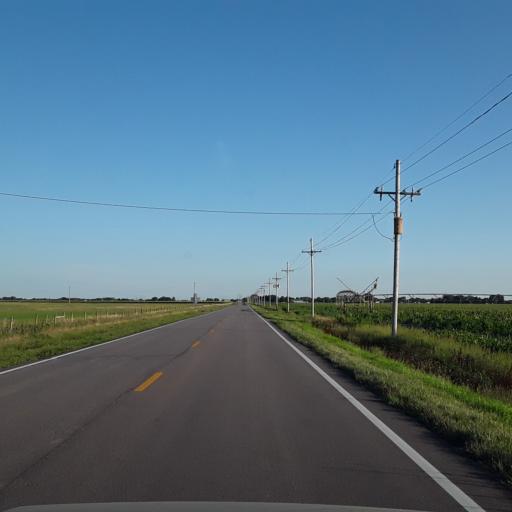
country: US
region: Nebraska
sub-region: Hall County
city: Grand Island
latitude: 40.9580
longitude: -98.3207
